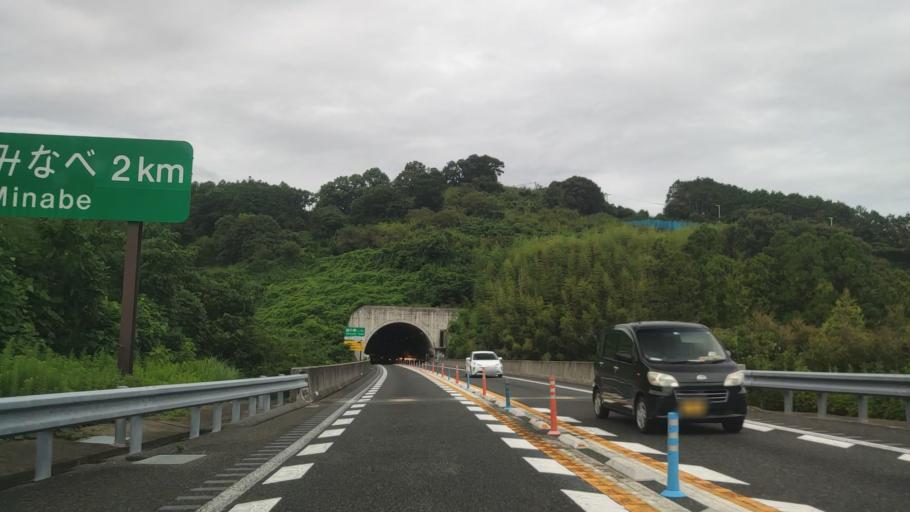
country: JP
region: Wakayama
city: Tanabe
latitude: 33.7668
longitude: 135.3503
